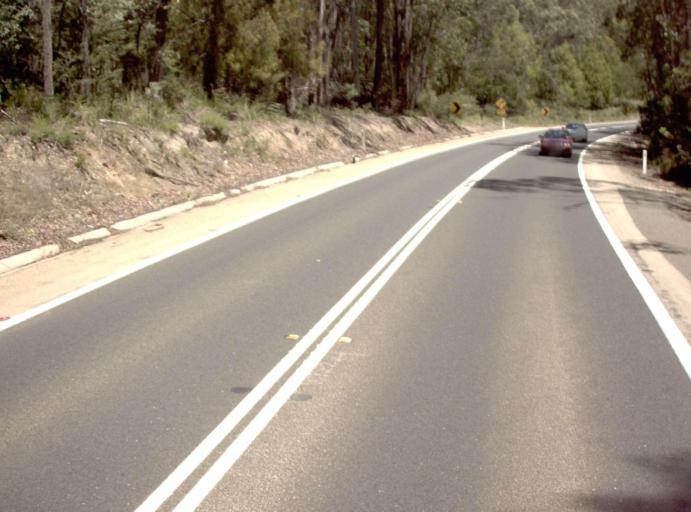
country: AU
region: Victoria
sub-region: East Gippsland
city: Lakes Entrance
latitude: -37.7049
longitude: 148.5769
